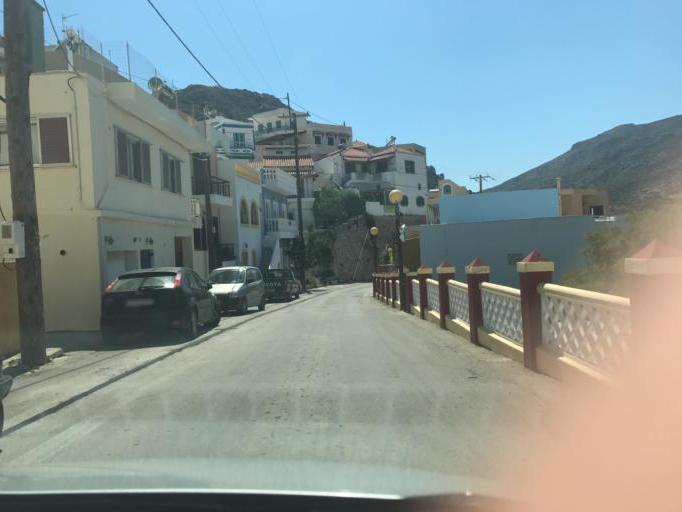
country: GR
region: South Aegean
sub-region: Nomos Dodekanisou
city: Karpathos
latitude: 35.4911
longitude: 27.1681
